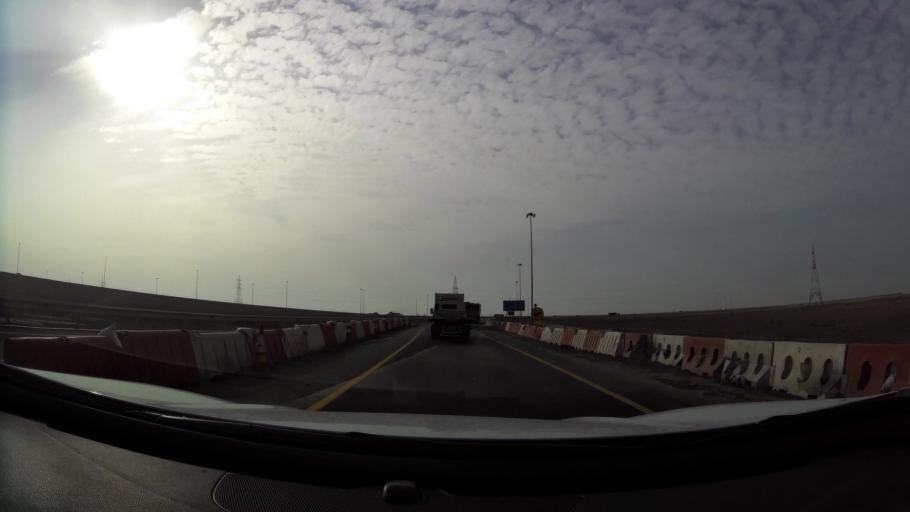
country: AE
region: Abu Dhabi
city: Abu Dhabi
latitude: 24.2161
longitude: 54.4166
